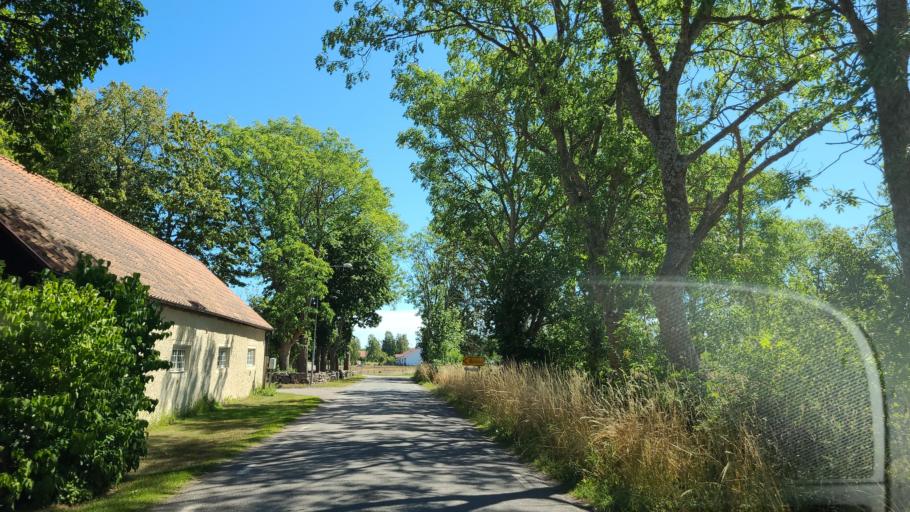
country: SE
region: Kalmar
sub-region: Borgholms Kommun
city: Borgholm
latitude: 56.7458
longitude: 16.6934
